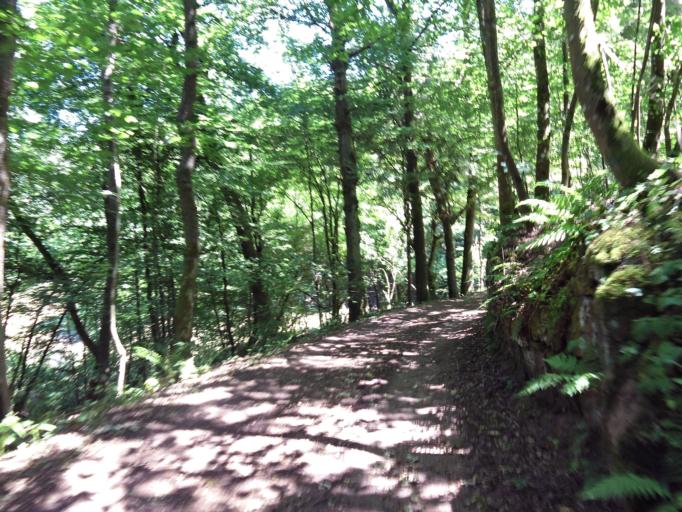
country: DE
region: Rheinland-Pfalz
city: Frankeneck
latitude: 49.3678
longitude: 8.0407
